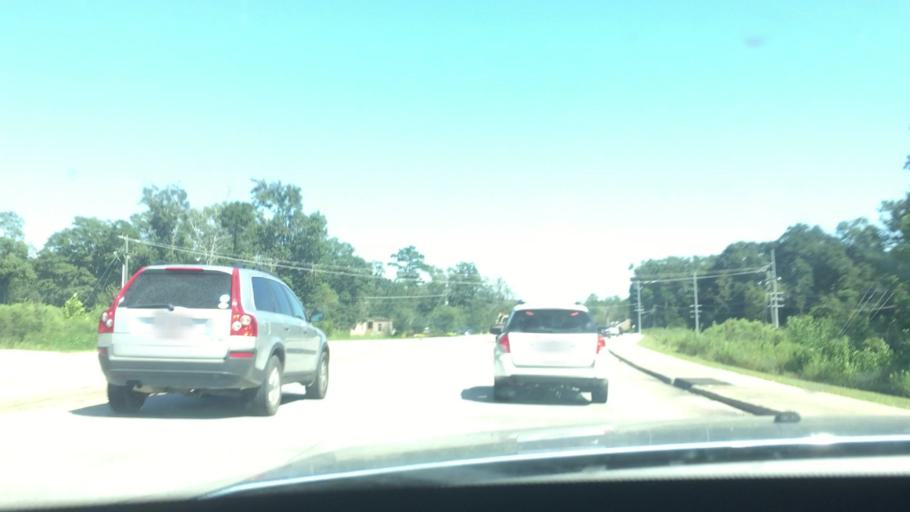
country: US
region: Louisiana
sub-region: East Baton Rouge Parish
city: Shenandoah
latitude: 30.4268
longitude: -91.0137
